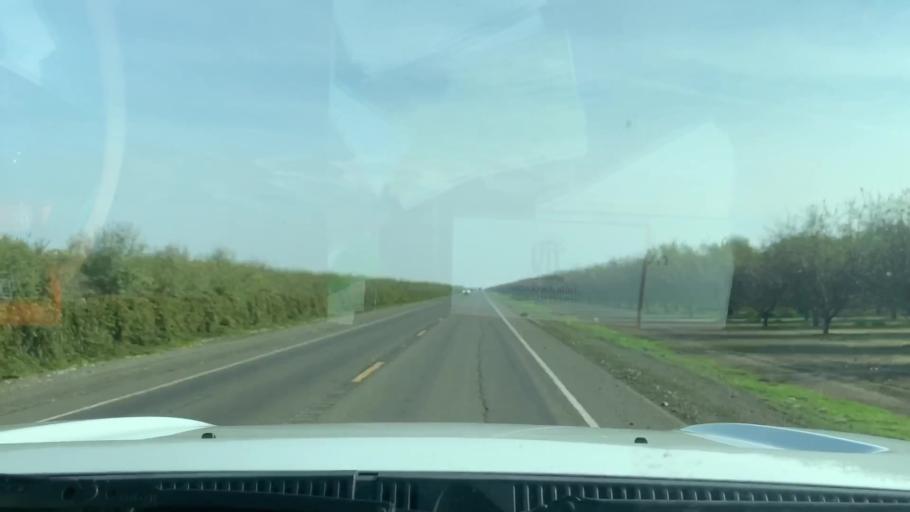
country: US
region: California
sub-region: Fresno County
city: Huron
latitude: 36.2552
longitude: -120.1352
